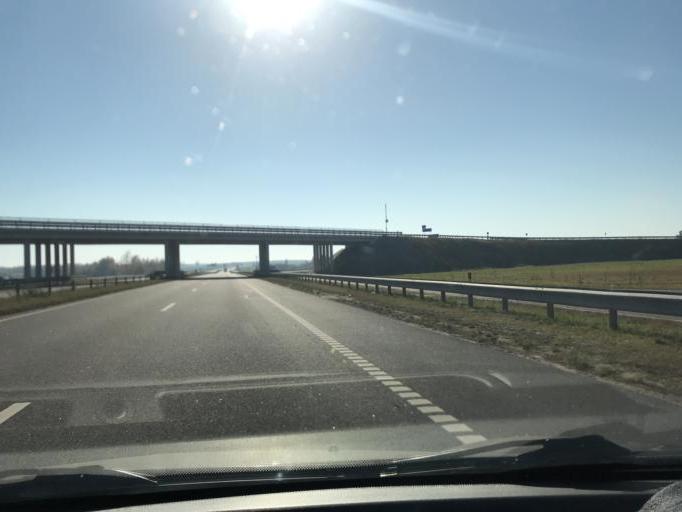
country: BY
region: Mogilev
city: Babruysk
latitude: 53.1864
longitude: 29.3554
